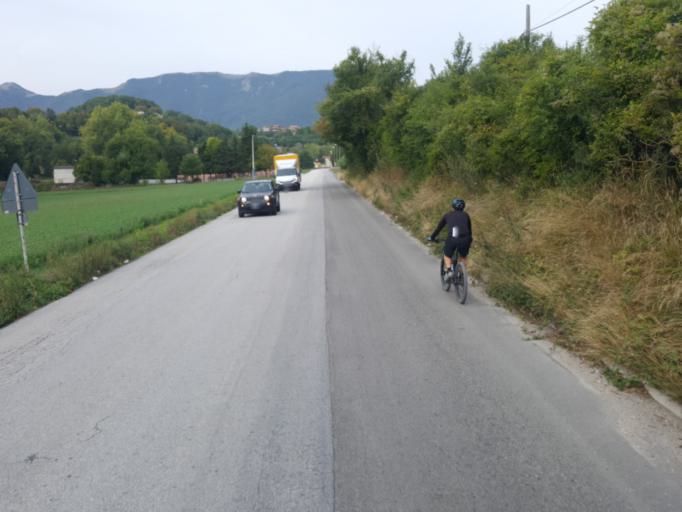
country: IT
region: The Marches
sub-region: Provincia di Ancona
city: Fabriano
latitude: 43.3462
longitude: 12.8545
